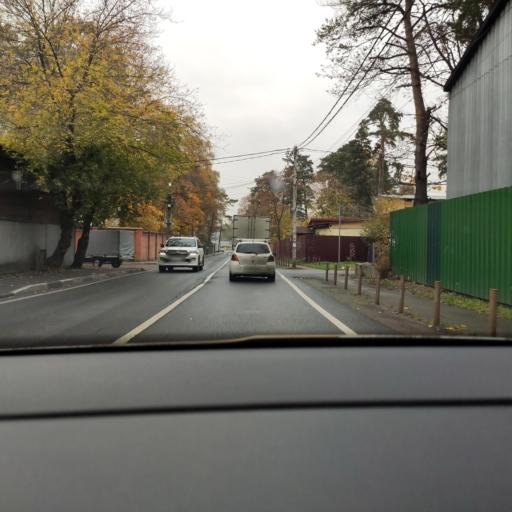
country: RU
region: Moskovskaya
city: Druzhba
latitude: 55.8863
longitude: 37.7397
